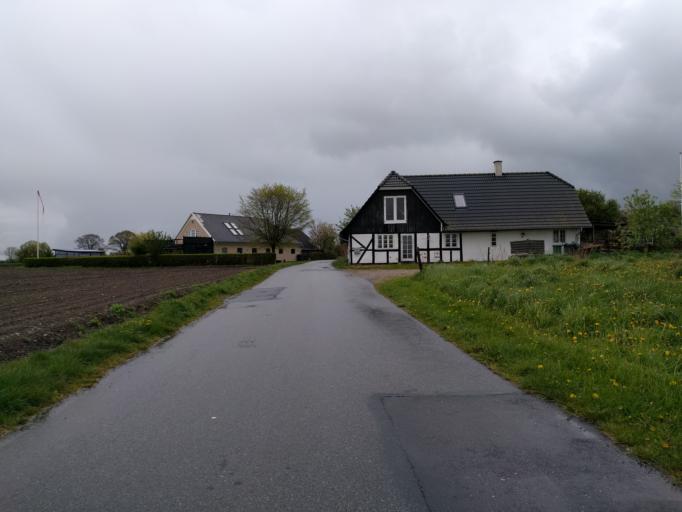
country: DK
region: South Denmark
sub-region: Kerteminde Kommune
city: Munkebo
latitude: 55.4286
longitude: 10.5879
